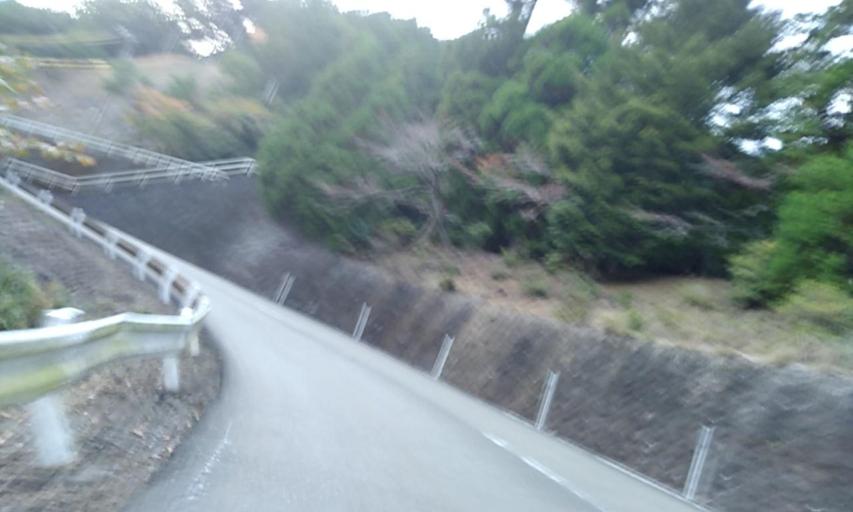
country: JP
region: Mie
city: Toba
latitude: 34.4560
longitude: 136.7859
